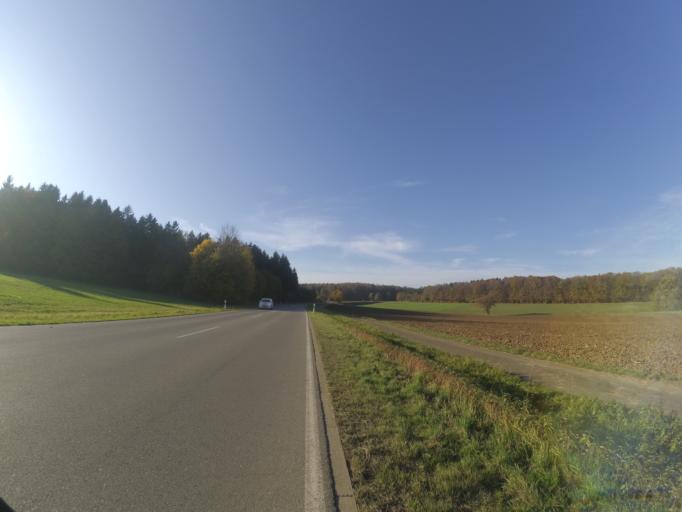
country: DE
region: Baden-Wuerttemberg
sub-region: Tuebingen Region
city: Blaubeuren
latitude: 48.4463
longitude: 9.8042
